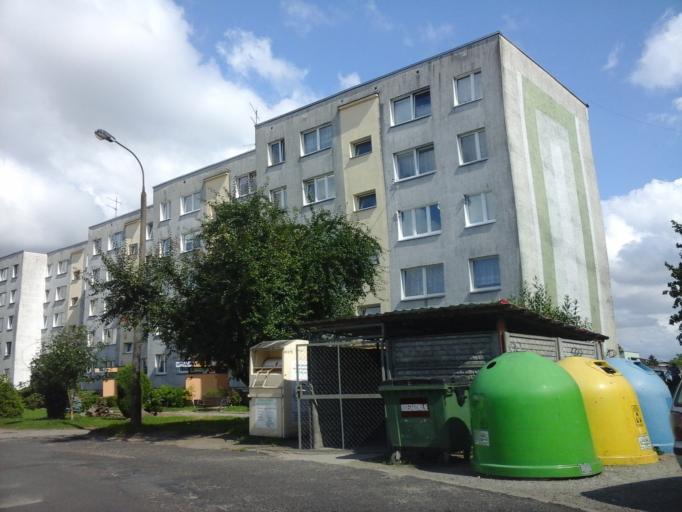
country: PL
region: West Pomeranian Voivodeship
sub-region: Powiat choszczenski
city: Choszczno
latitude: 53.1662
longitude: 15.4276
